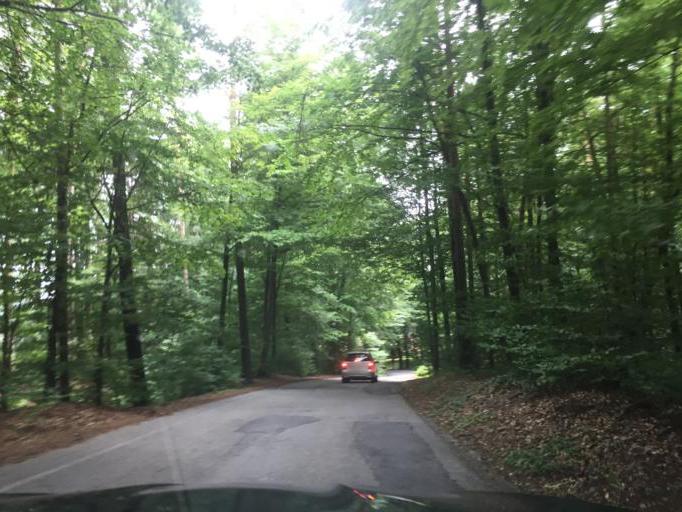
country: AT
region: Styria
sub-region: Politischer Bezirk Graz-Umgebung
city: Hart bei Graz
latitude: 47.0554
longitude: 15.5127
